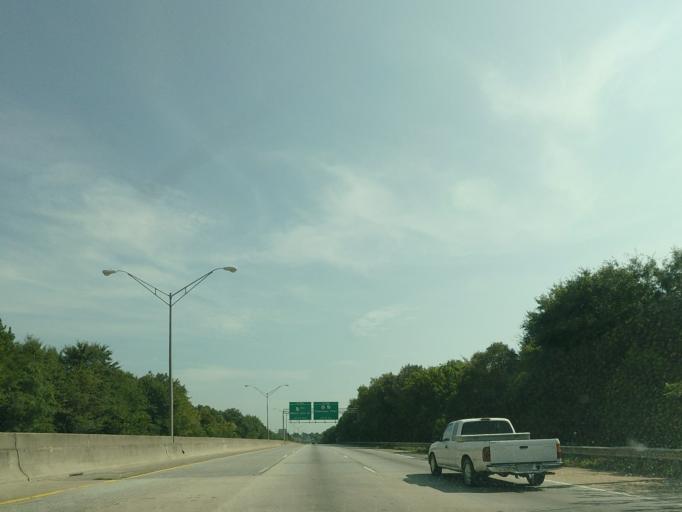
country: US
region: Georgia
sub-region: Bibb County
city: Macon
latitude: 32.8033
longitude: -83.6586
